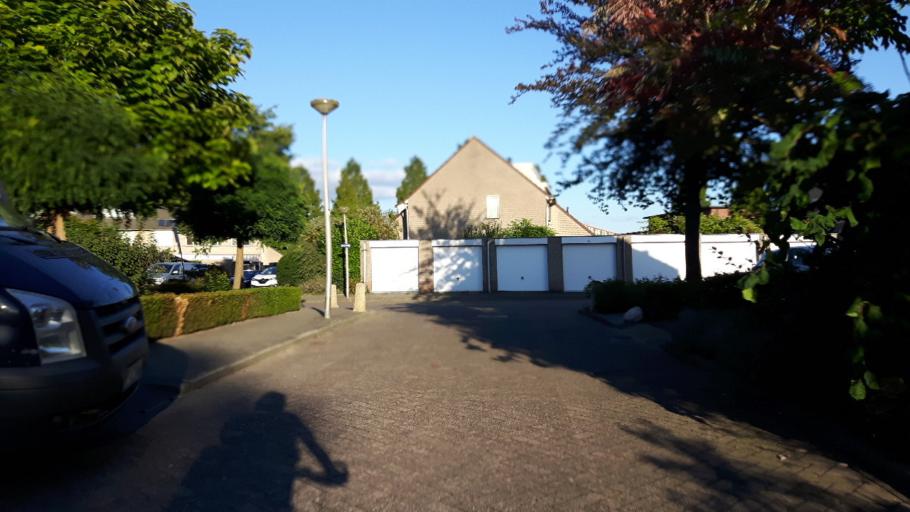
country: NL
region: Utrecht
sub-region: Gemeente Oudewater
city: Oudewater
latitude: 52.0270
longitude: 4.8723
